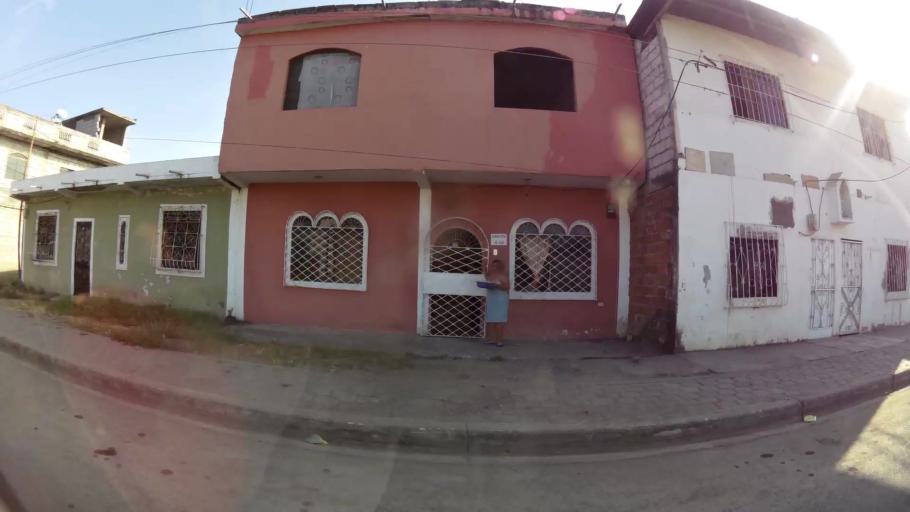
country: EC
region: Guayas
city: Eloy Alfaro
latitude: -2.1862
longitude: -79.8461
